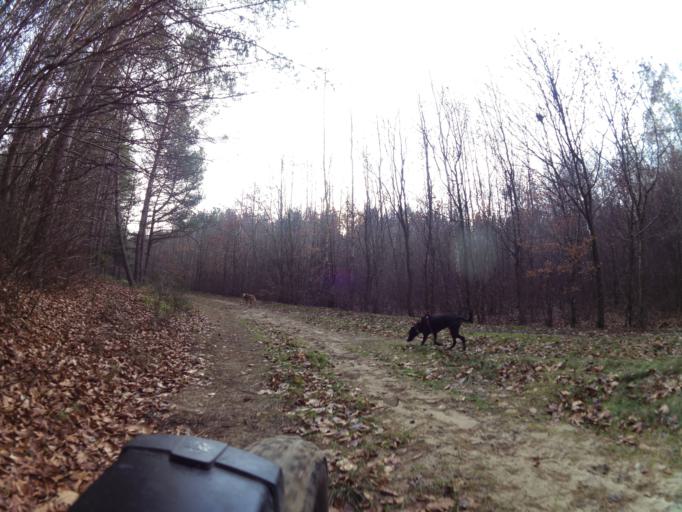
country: PL
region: West Pomeranian Voivodeship
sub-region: Powiat koszalinski
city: Polanow
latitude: 54.1873
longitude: 16.7286
